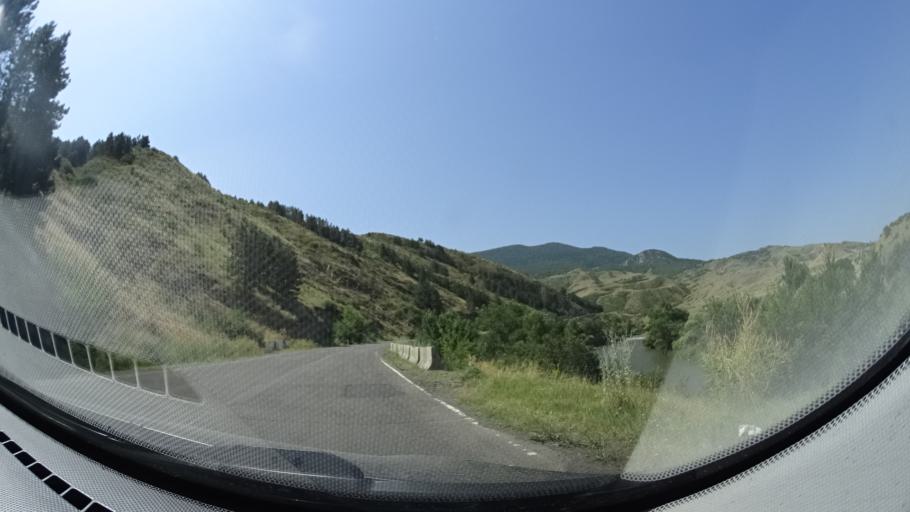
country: GE
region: Samtskhe-Javakheti
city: Aspindza
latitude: 41.6107
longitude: 43.1407
